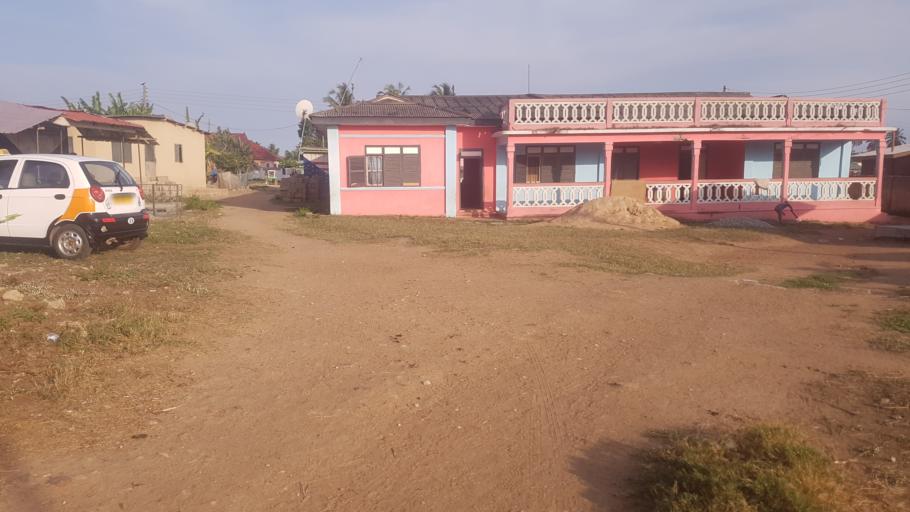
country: GH
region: Central
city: Winneba
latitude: 5.3540
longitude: -0.6302
